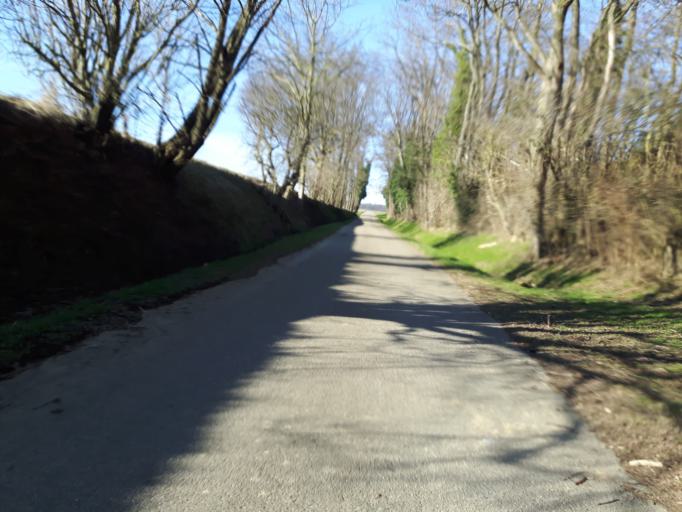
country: DE
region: Baden-Wuerttemberg
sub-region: Regierungsbezirk Stuttgart
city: Leingarten
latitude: 49.1537
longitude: 9.0997
